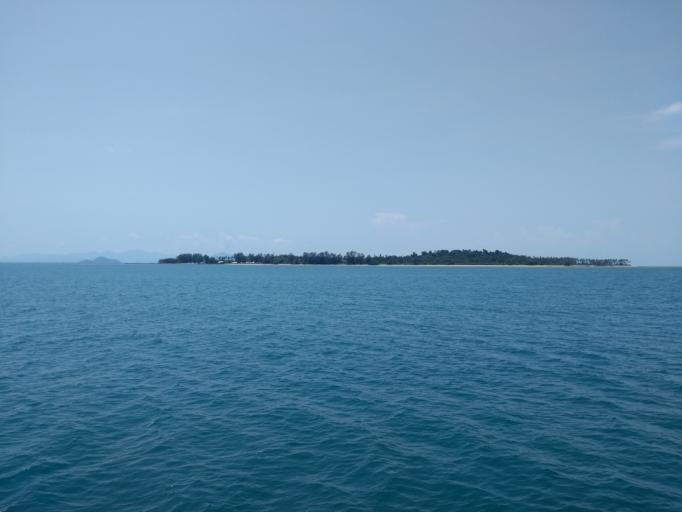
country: TH
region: Trat
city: Ko Kut
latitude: 11.8199
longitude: 102.5300
